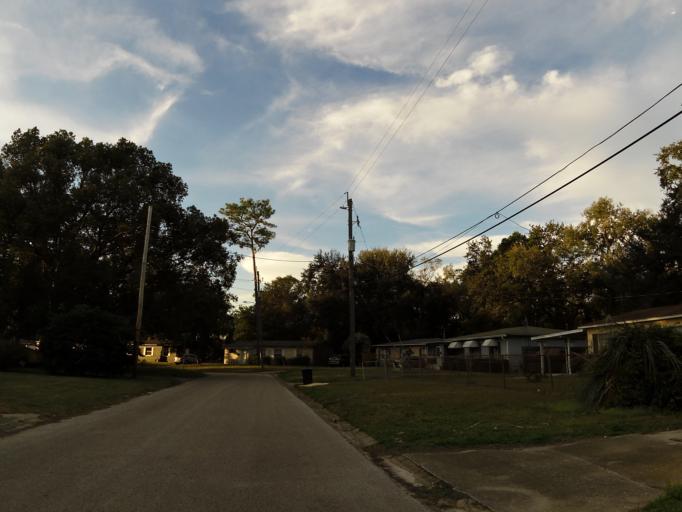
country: US
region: Florida
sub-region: Duval County
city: Jacksonville
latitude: 30.2896
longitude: -81.6384
